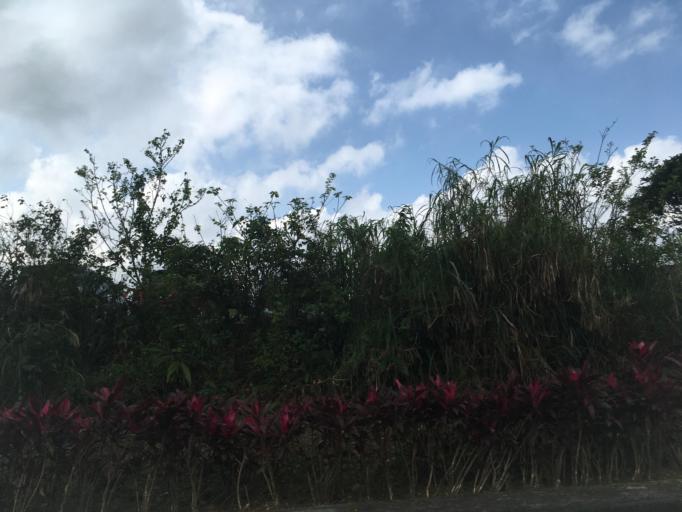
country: TW
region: Taiwan
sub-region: Keelung
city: Keelung
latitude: 25.0156
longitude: 121.9474
